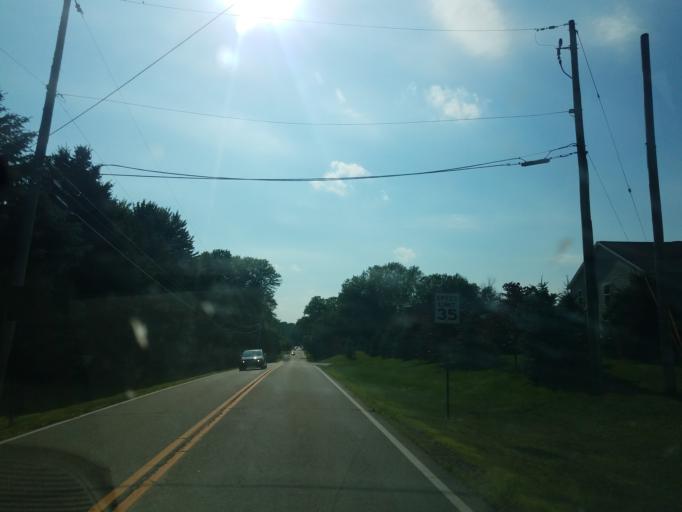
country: US
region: Ohio
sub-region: Stark County
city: Uniontown
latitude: 40.9507
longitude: -81.4297
